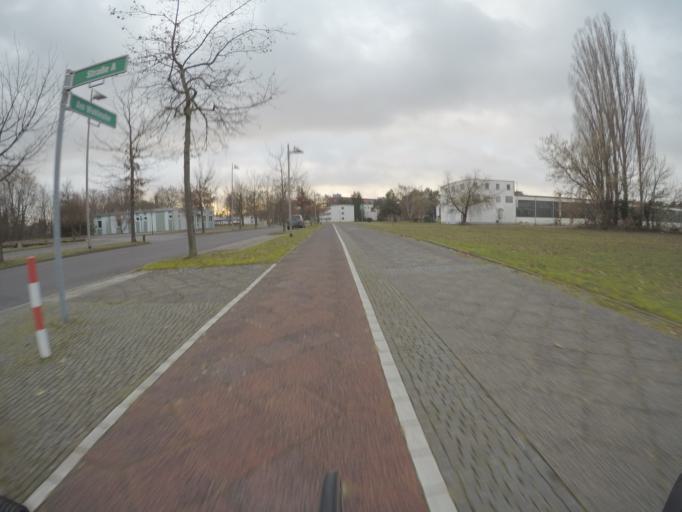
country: DE
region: Berlin
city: Kopenick Bezirk
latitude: 52.4699
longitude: 13.5655
